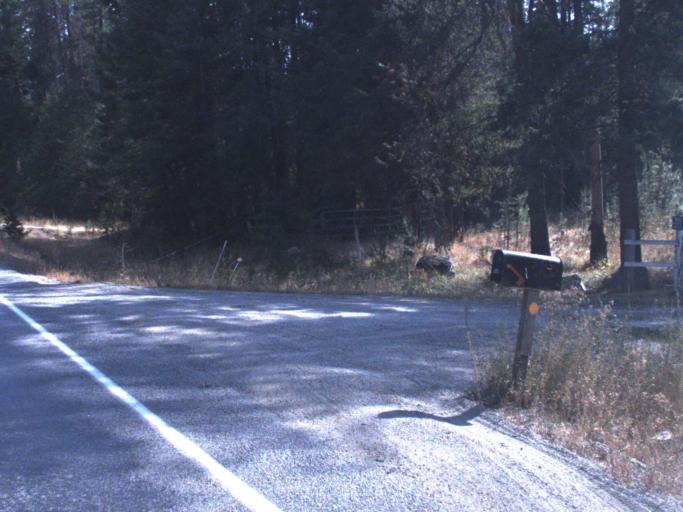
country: US
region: Washington
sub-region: Pend Oreille County
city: Newport
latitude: 48.1241
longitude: -117.2739
